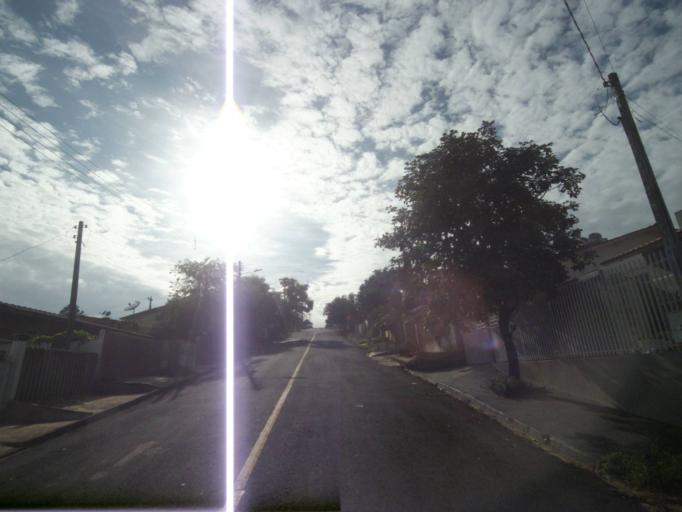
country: BR
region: Parana
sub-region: Telemaco Borba
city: Telemaco Borba
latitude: -24.3451
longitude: -50.6092
